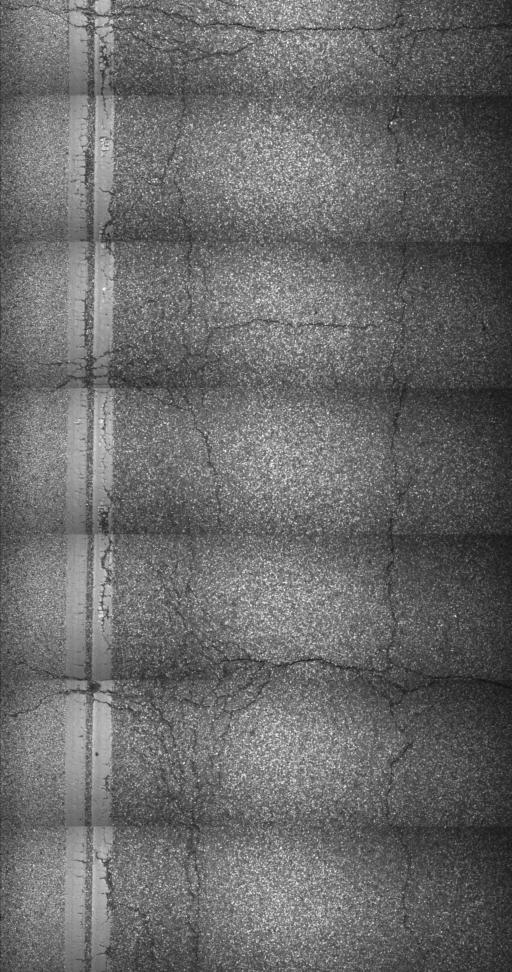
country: US
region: Vermont
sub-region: Windham County
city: Newfane
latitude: 43.0793
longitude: -72.7419
